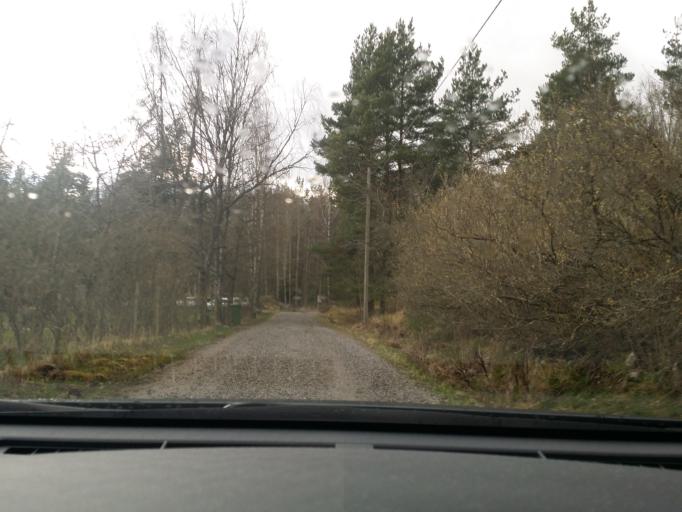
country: SE
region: Soedermanland
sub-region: Eskilstuna Kommun
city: Arla
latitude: 59.3737
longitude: 16.6608
